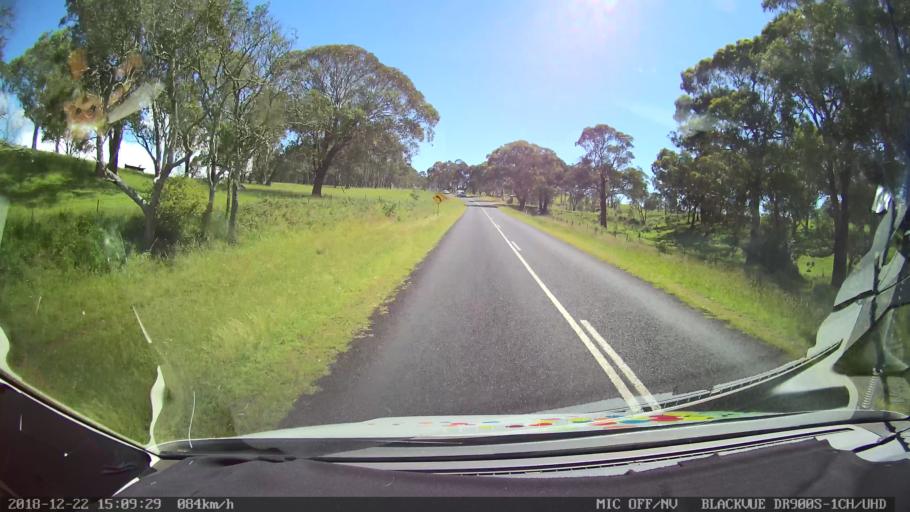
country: AU
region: New South Wales
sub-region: Bellingen
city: Dorrigo
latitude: -30.3244
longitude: 152.4084
